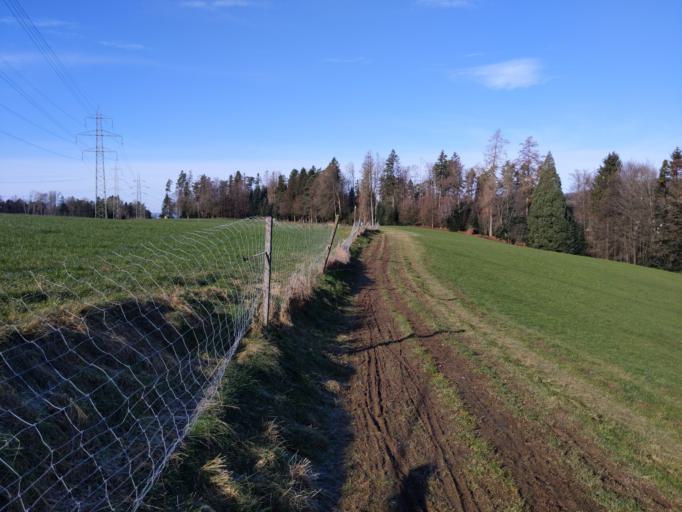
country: CH
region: Saint Gallen
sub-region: Wahlkreis See-Gaster
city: Schmerikon
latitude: 47.2320
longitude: 8.9391
